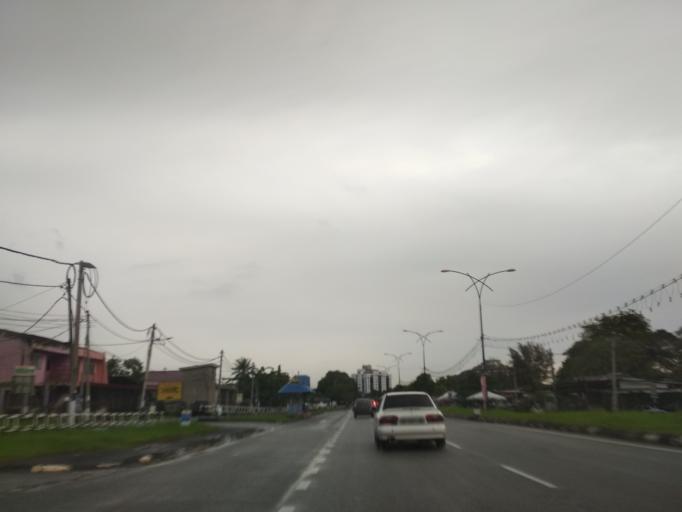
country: MY
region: Perlis
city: Kangar
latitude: 6.4503
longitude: 100.2059
